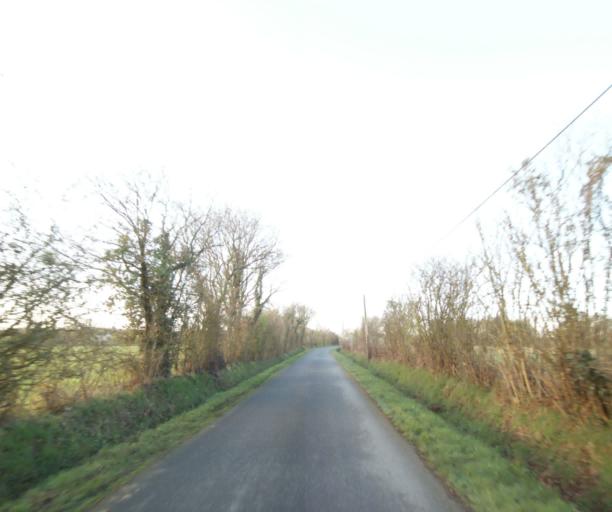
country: FR
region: Pays de la Loire
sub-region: Departement de la Loire-Atlantique
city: Bouvron
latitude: 47.4208
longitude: -1.8650
